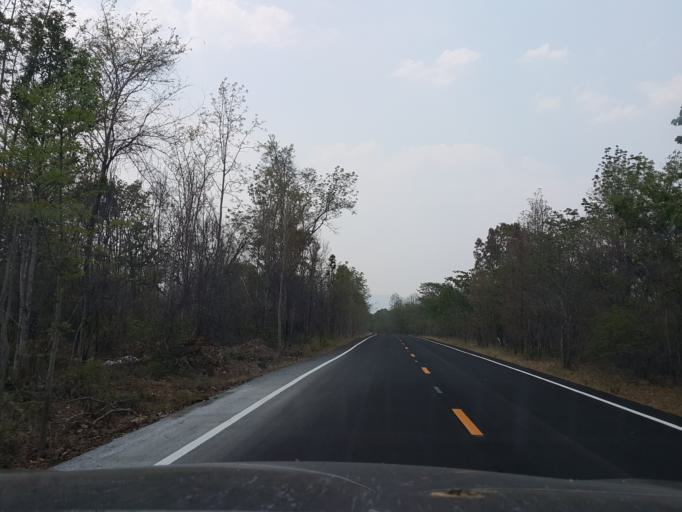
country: TH
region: Lampang
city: Mae Phrik
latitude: 17.4838
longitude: 99.1078
